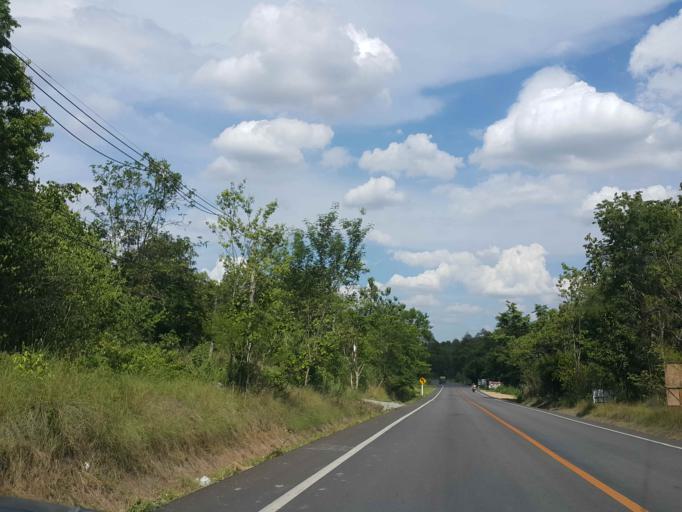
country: TH
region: Chiang Mai
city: San Sai
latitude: 18.9197
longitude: 98.9304
